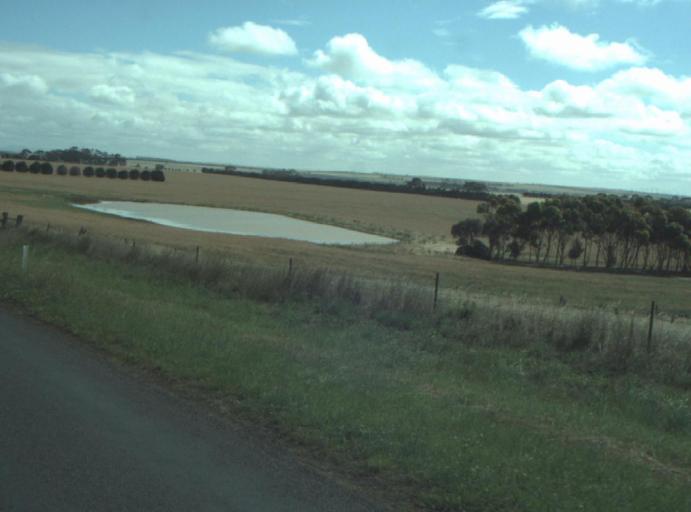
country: AU
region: Victoria
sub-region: Greater Geelong
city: Lara
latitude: -37.9356
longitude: 144.3107
